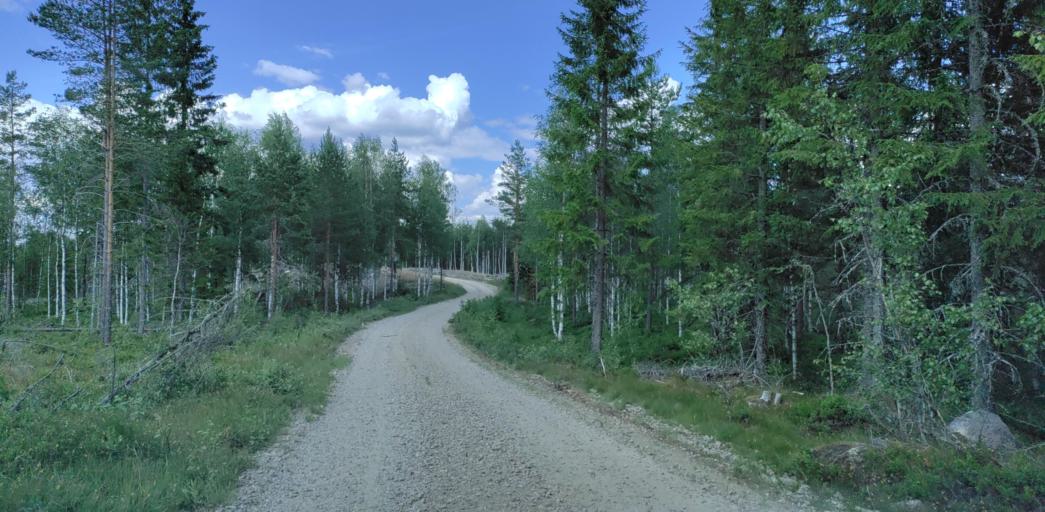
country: SE
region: Vaermland
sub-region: Hagfors Kommun
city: Ekshaerad
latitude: 60.0754
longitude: 13.3459
